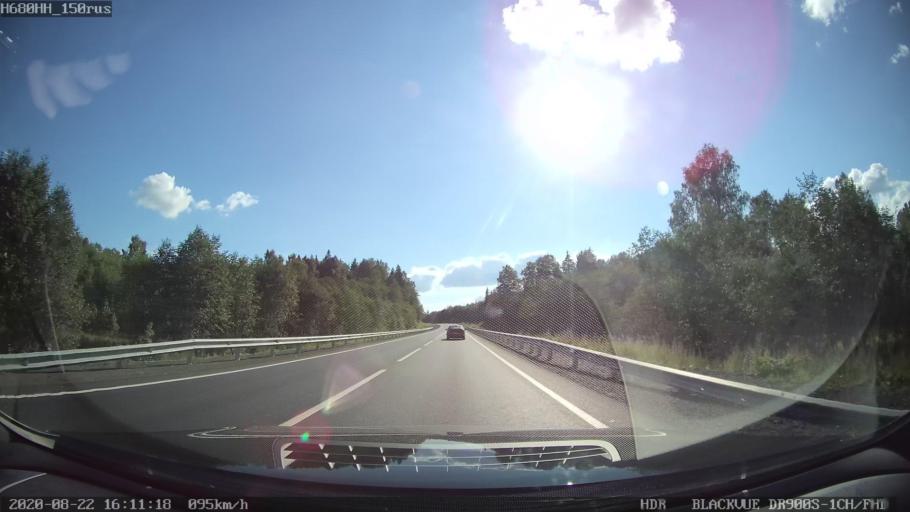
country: RU
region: Tverskaya
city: Rameshki
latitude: 57.5029
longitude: 36.2631
